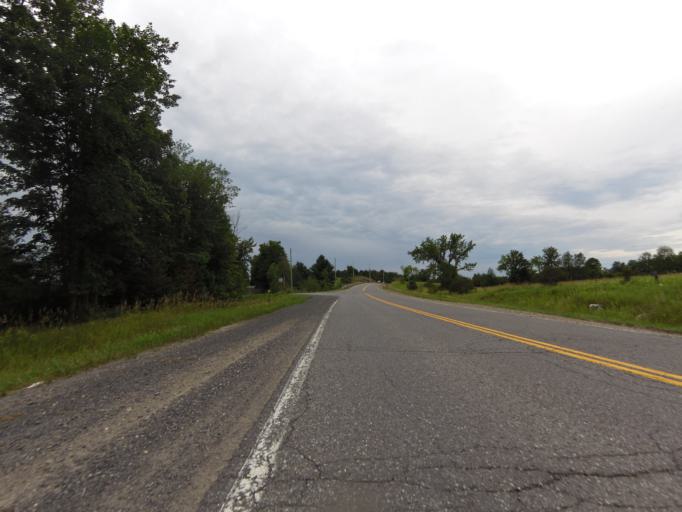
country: CA
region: Ontario
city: Carleton Place
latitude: 45.1316
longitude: -76.3311
